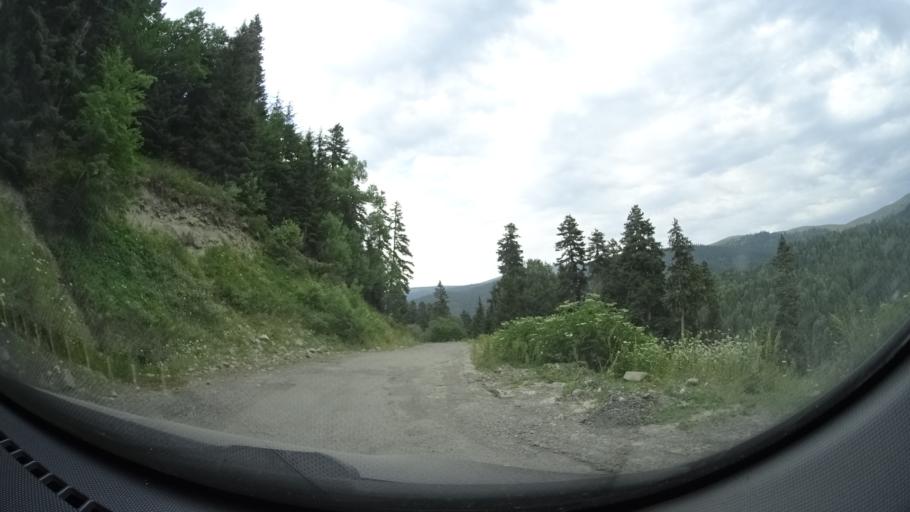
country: GE
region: Samtskhe-Javakheti
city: Adigeni
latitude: 41.6375
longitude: 42.5805
